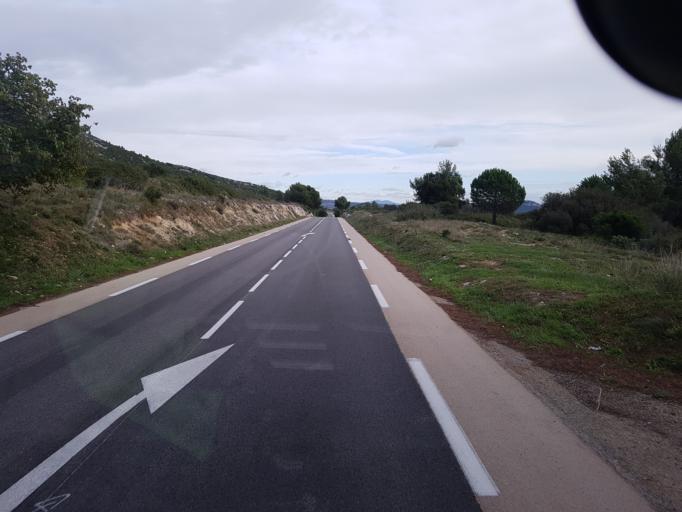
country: FR
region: Provence-Alpes-Cote d'Azur
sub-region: Departement des Bouches-du-Rhone
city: La Penne-sur-Huveaune
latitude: 43.2392
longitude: 5.4750
